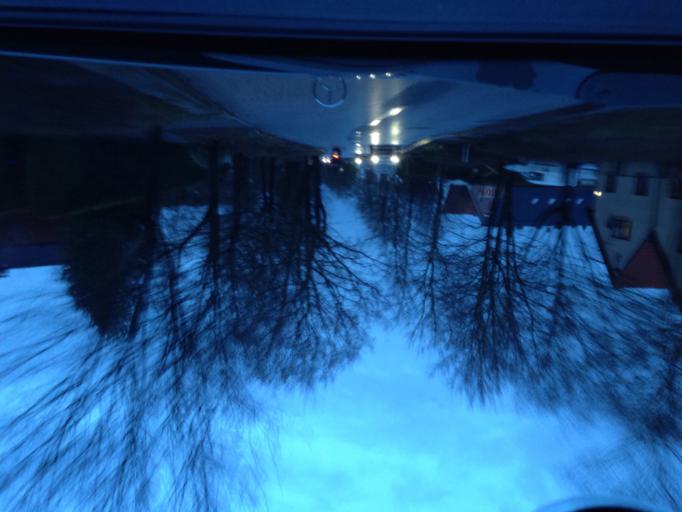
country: DE
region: Hamburg
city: Farmsen-Berne
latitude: 53.6096
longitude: 10.1413
